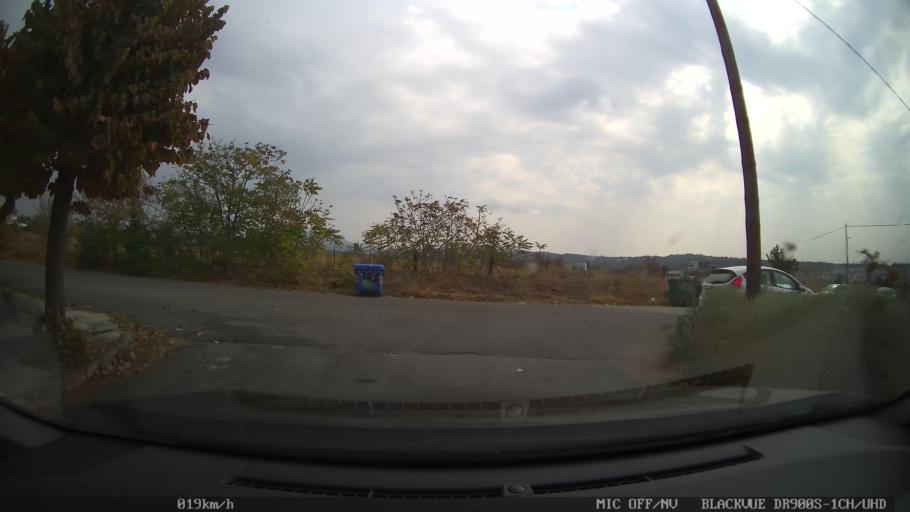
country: GR
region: Central Macedonia
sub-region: Nomos Thessalonikis
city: Pylaia
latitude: 40.6109
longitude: 22.9976
